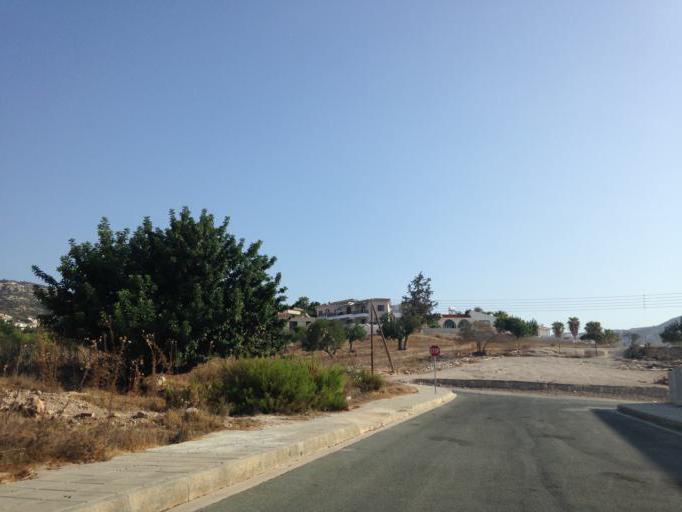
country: CY
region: Pafos
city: Pegeia
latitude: 34.8793
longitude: 32.3831
